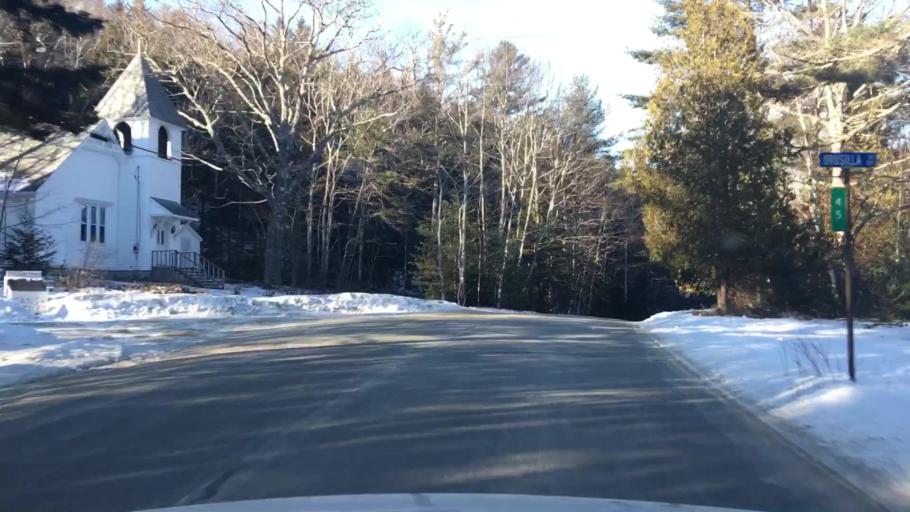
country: US
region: Maine
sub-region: Hancock County
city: Castine
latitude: 44.3440
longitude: -68.7829
